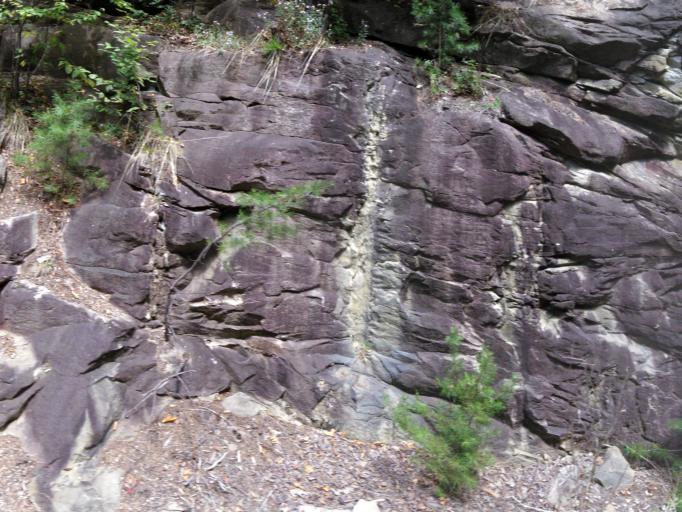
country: US
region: Kentucky
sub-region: Harlan County
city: Harlan
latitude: 36.8814
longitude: -83.3116
